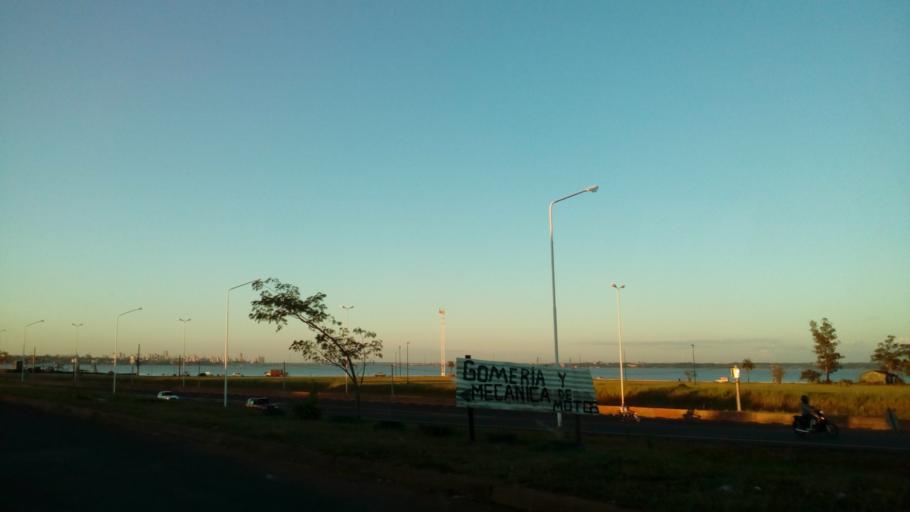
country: AR
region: Misiones
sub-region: Departamento de Capital
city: Posadas
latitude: -27.4238
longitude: -55.8762
